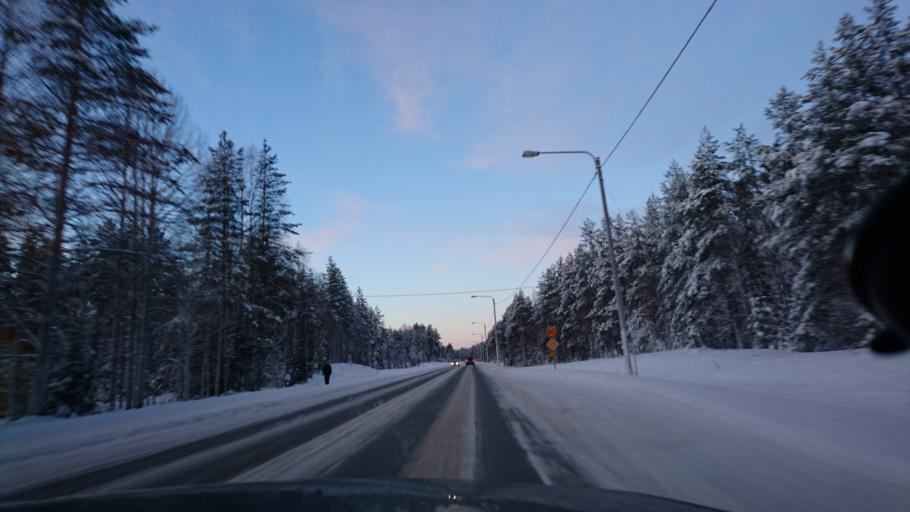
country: FI
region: Lapland
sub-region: Rovaniemi
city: Ranua
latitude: 65.9406
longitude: 26.4803
